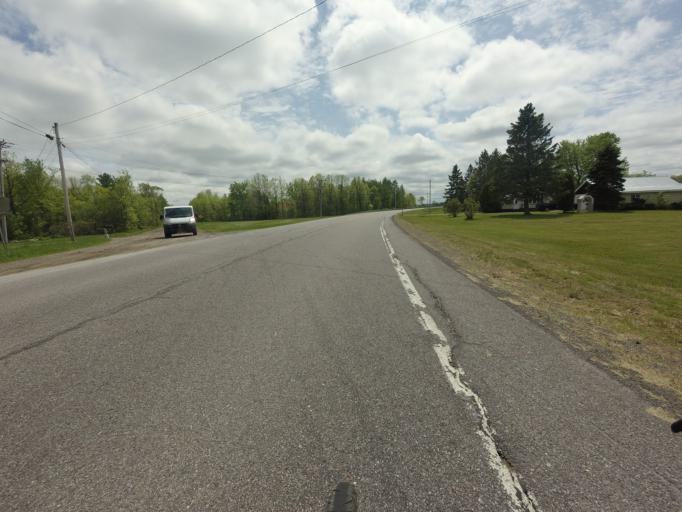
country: CA
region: Ontario
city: Cornwall
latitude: 44.9612
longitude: -74.6665
